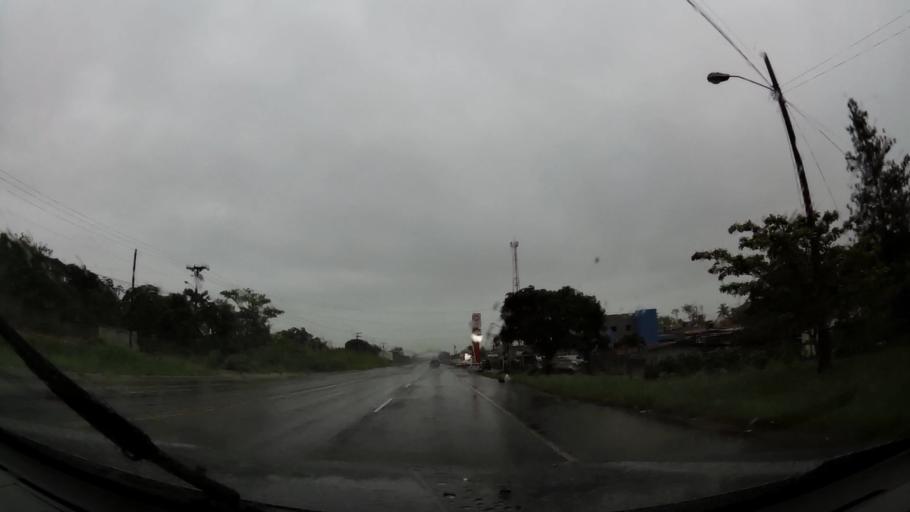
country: PA
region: Colon
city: Sabanitas
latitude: 9.3393
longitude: -79.8046
